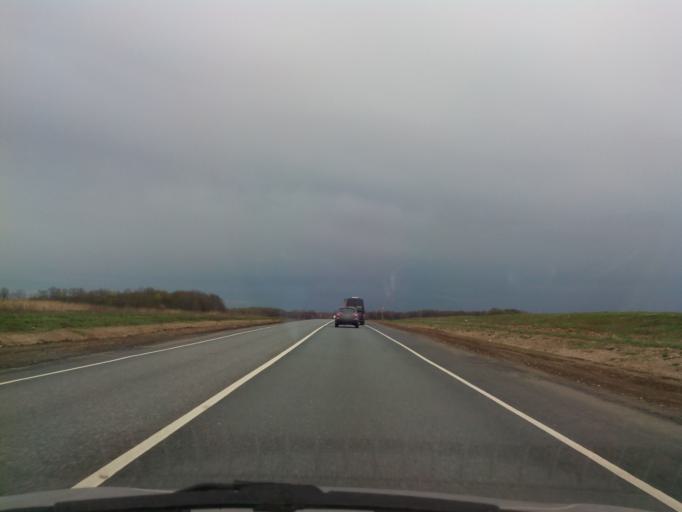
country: RU
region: Moskovskaya
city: Uzunovo
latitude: 54.5425
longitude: 38.4691
